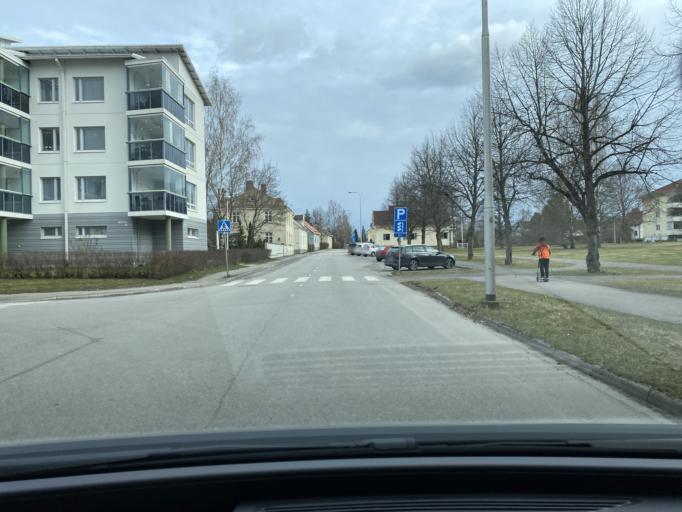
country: FI
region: Pirkanmaa
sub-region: Lounais-Pirkanmaa
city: Vammala
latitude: 61.3395
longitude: 22.9084
